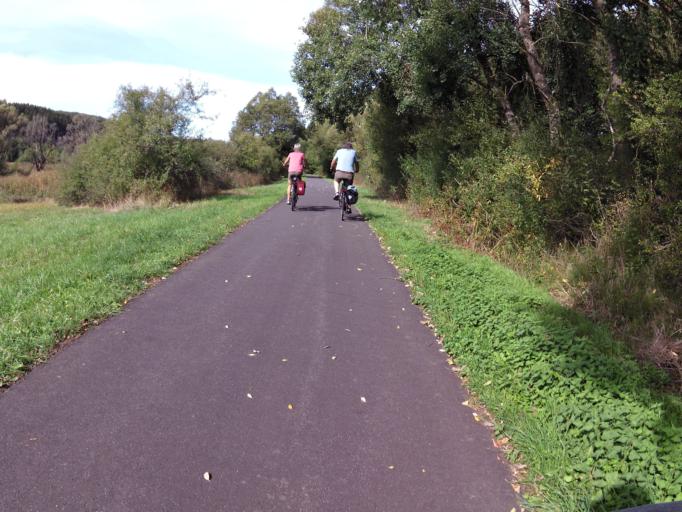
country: DE
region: Rheinland-Pfalz
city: Pronsfeld
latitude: 50.1743
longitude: 6.3169
